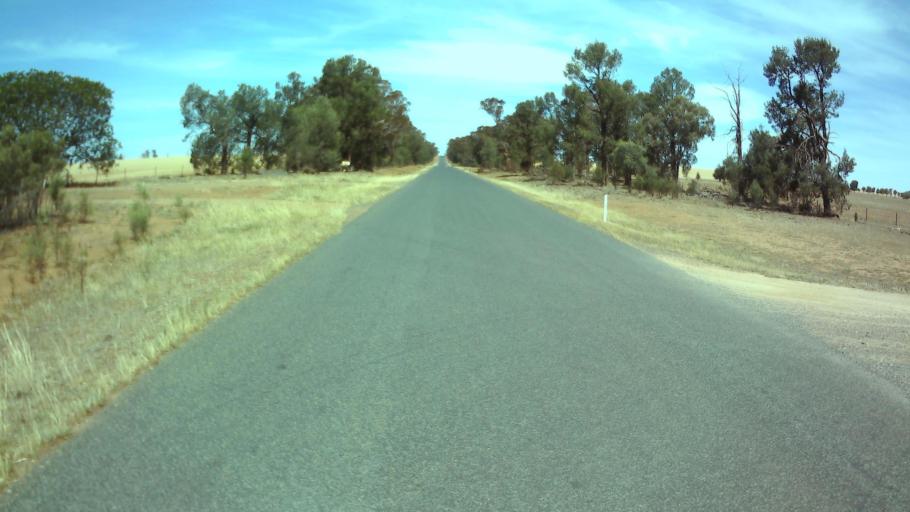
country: AU
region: New South Wales
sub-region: Weddin
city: Grenfell
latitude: -33.8944
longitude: 147.7480
